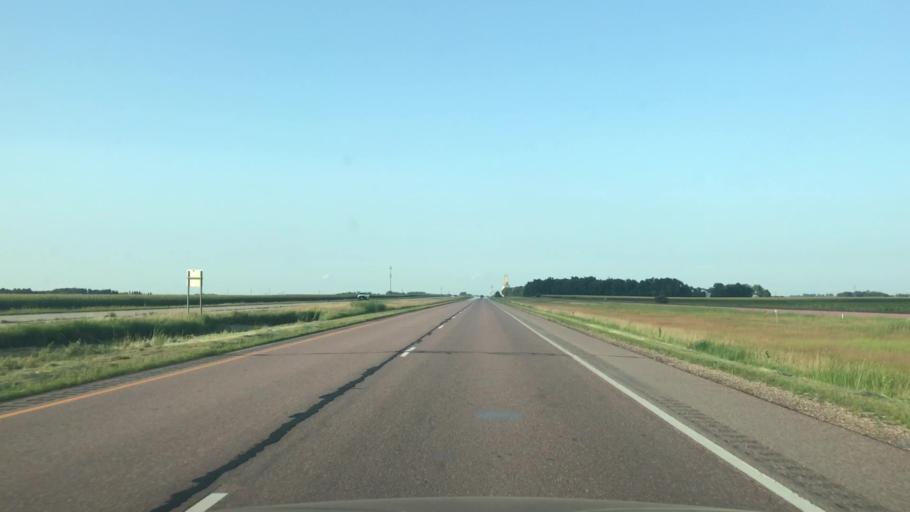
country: US
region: Minnesota
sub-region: Jackson County
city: Lakefield
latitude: 43.7538
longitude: -95.3864
